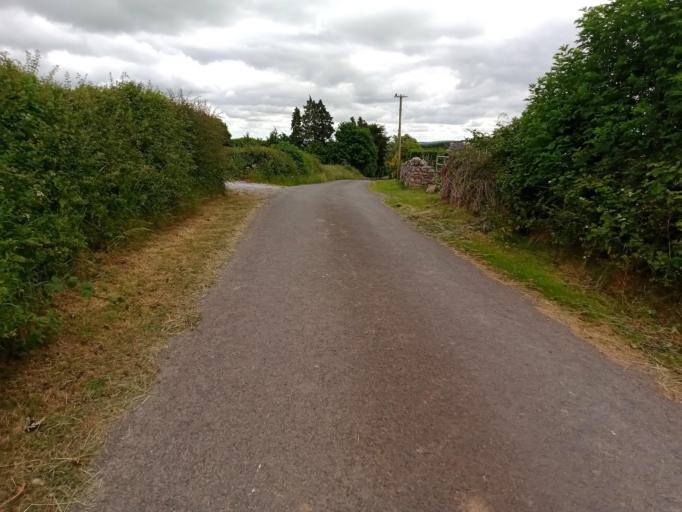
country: IE
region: Leinster
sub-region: Laois
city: Rathdowney
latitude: 52.7853
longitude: -7.4776
